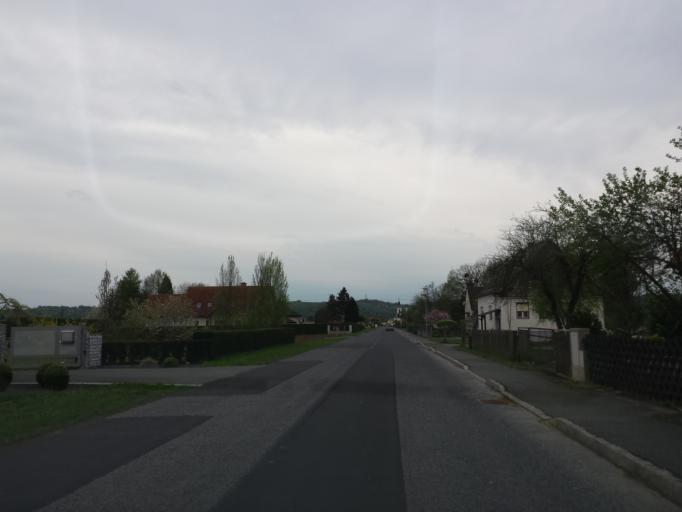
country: AT
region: Burgenland
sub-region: Politischer Bezirk Jennersdorf
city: Konigsdorf
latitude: 47.0107
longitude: 16.1756
